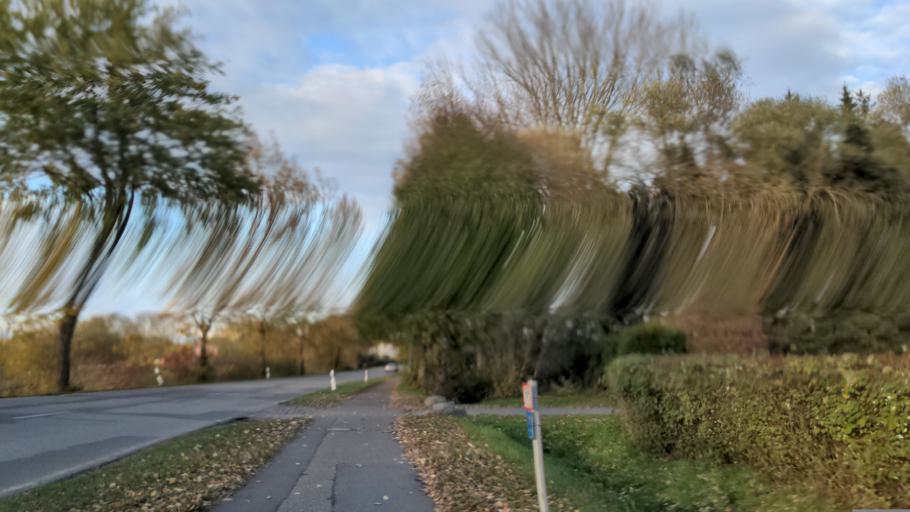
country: DE
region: Schleswig-Holstein
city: Heidekamp
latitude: 53.8453
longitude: 10.4999
